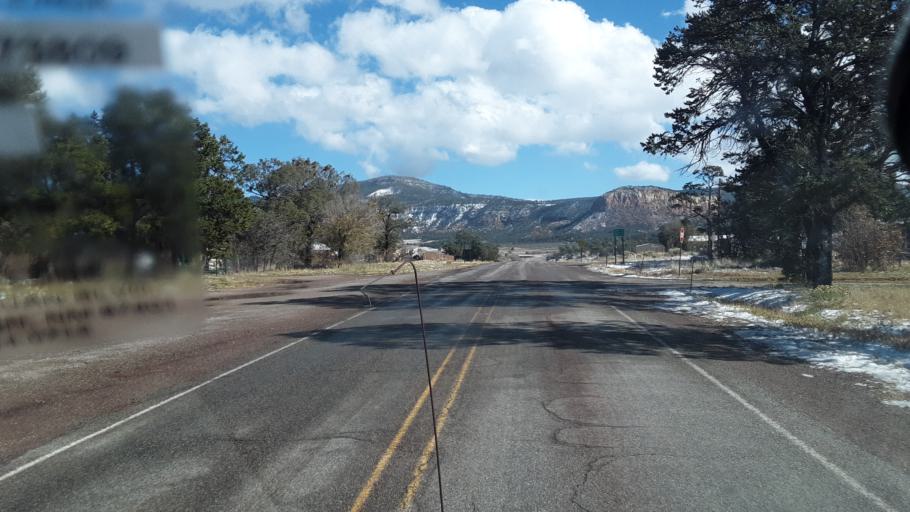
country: US
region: New Mexico
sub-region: Rio Arriba County
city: Santa Teresa
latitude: 36.2289
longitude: -106.8177
